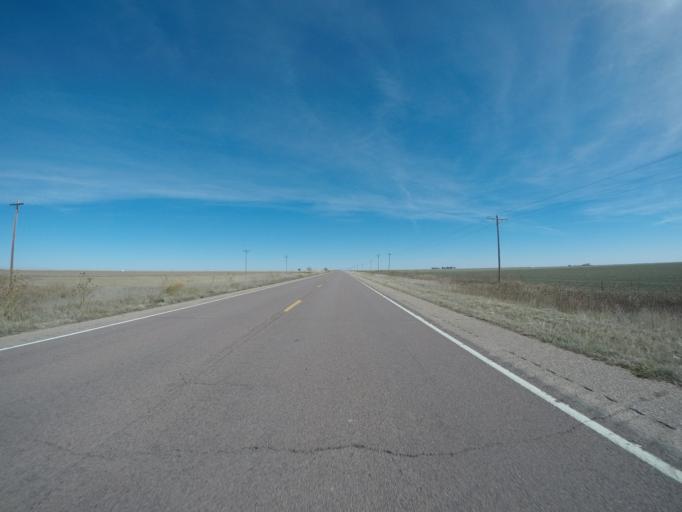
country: US
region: Colorado
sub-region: Kit Carson County
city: Burlington
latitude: 39.6574
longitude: -102.4514
